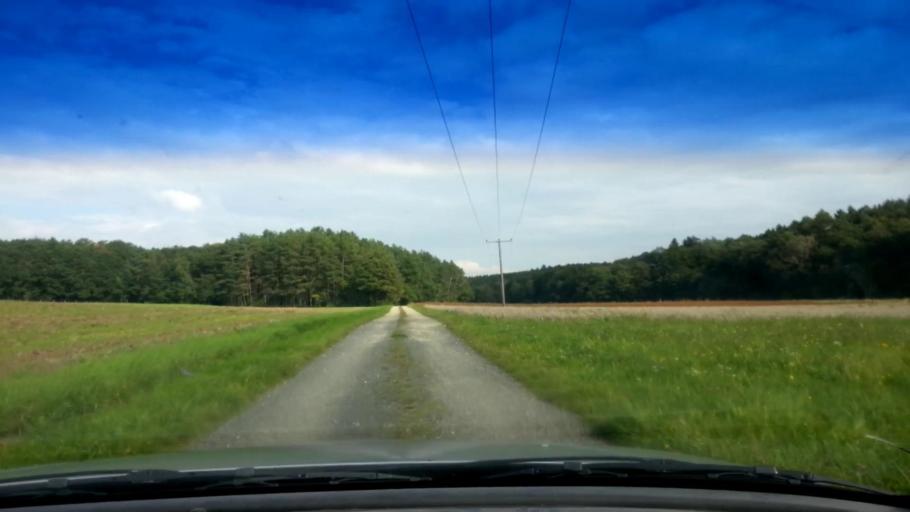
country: DE
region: Bavaria
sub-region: Upper Franconia
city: Gundelsheim
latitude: 49.9691
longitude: 10.9303
